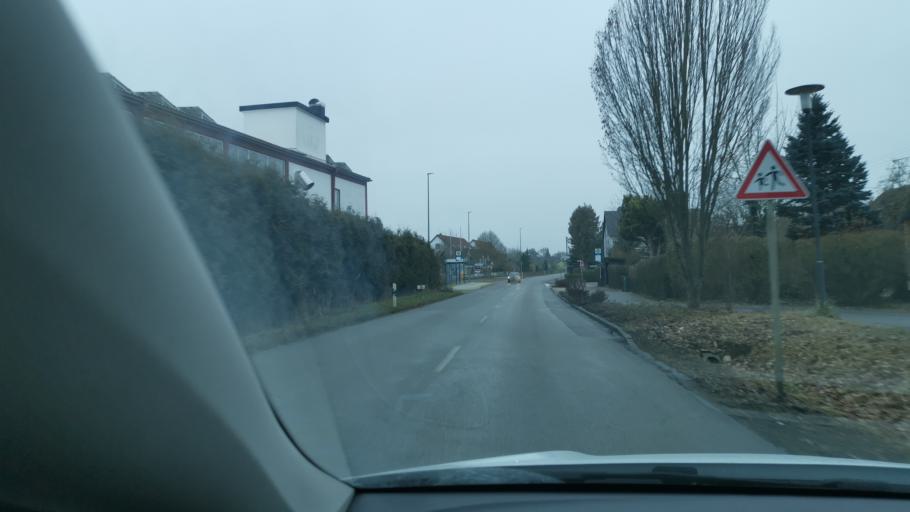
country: DE
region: Bavaria
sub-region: Swabia
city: Holzheim
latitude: 48.5893
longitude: 10.9600
